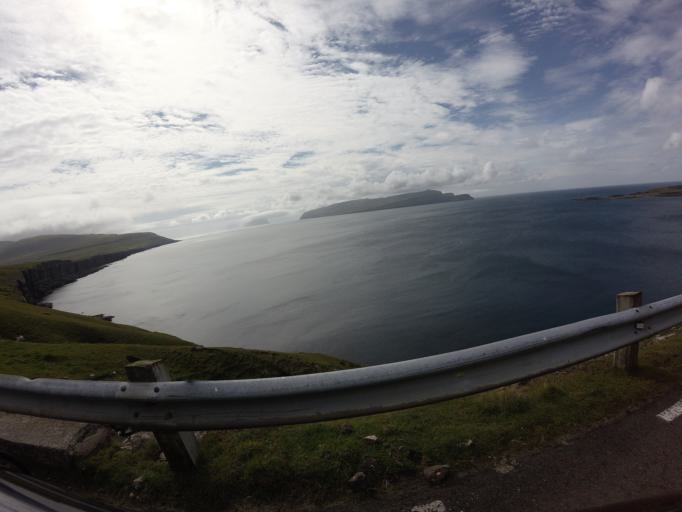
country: FO
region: Sandoy
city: Sandur
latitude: 61.8323
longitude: -6.7791
